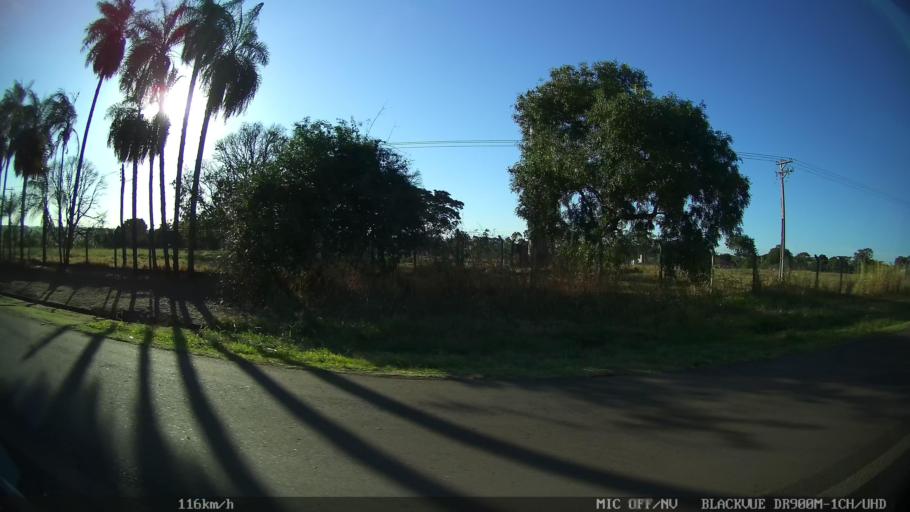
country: BR
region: Sao Paulo
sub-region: Guapiacu
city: Guapiacu
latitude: -20.7869
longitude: -49.2820
